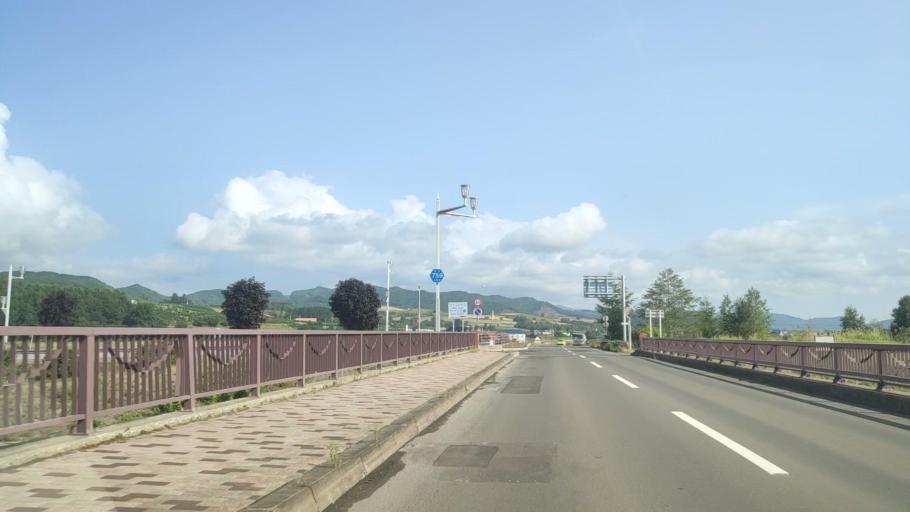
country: JP
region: Hokkaido
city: Shimo-furano
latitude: 43.3575
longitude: 142.3826
